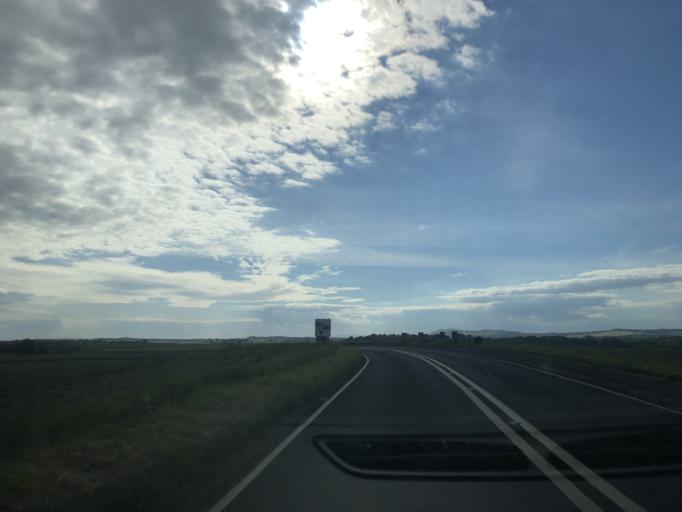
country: GB
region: Scotland
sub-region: Fife
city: Pittenweem
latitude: 56.2133
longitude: -2.7414
